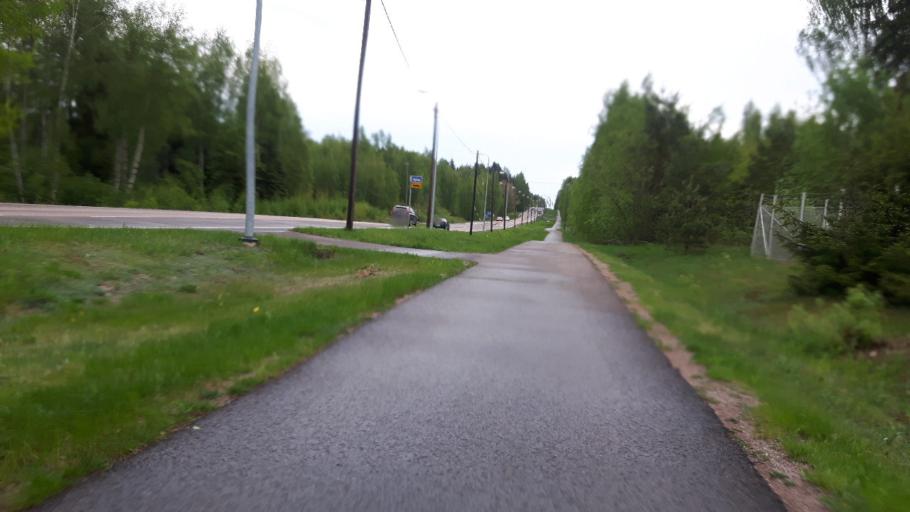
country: FI
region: Kymenlaakso
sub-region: Kotka-Hamina
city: Hamina
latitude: 60.5645
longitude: 27.1376
